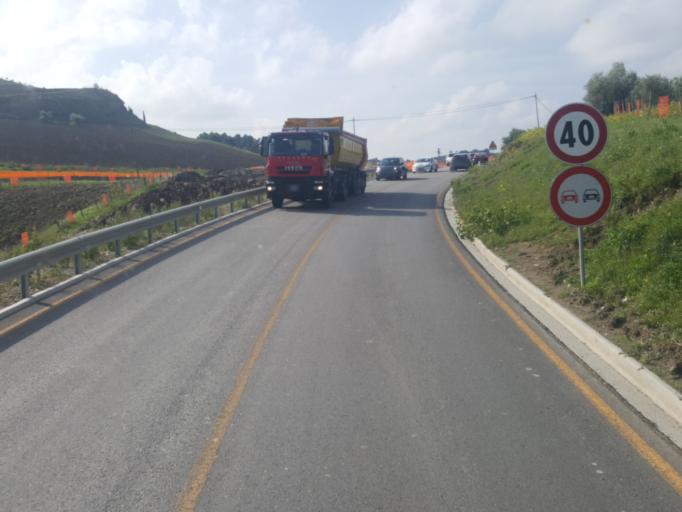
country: IT
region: Sicily
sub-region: Provincia di Caltanissetta
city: San Cataldo
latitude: 37.4484
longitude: 13.9582
